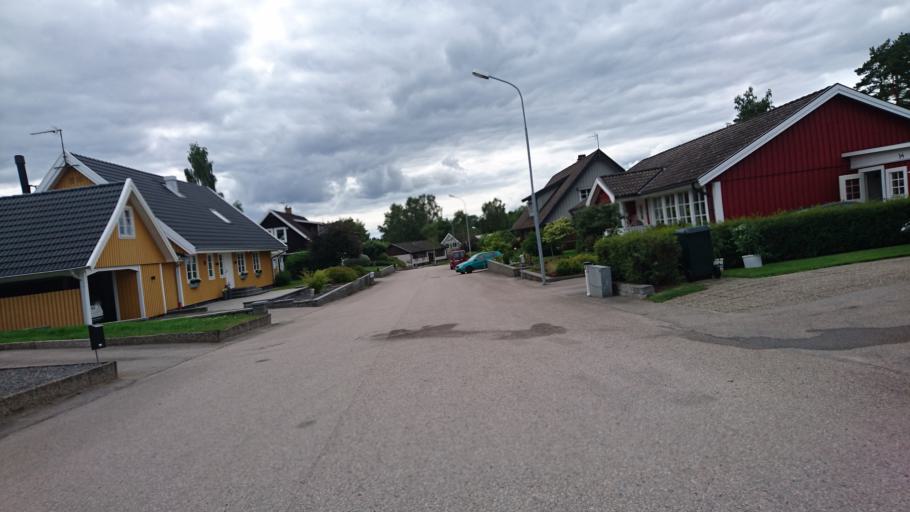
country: SE
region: Kronoberg
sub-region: Alvesta Kommun
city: Moheda
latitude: 56.9944
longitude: 14.5843
